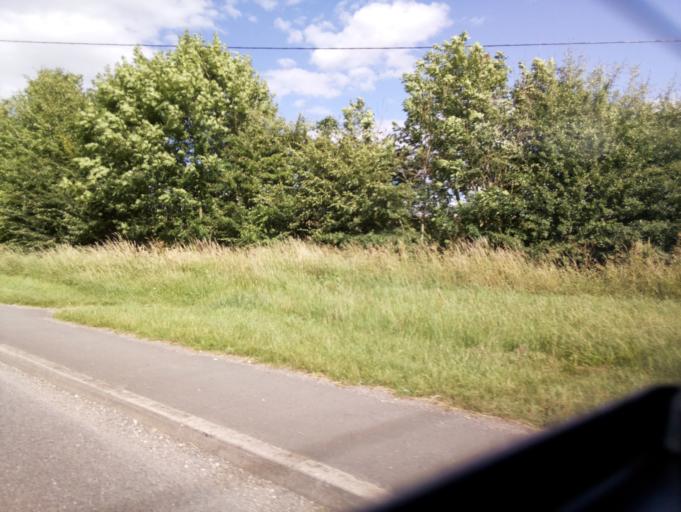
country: GB
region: England
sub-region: Leicestershire
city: Hathern
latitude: 52.8013
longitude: -1.2610
